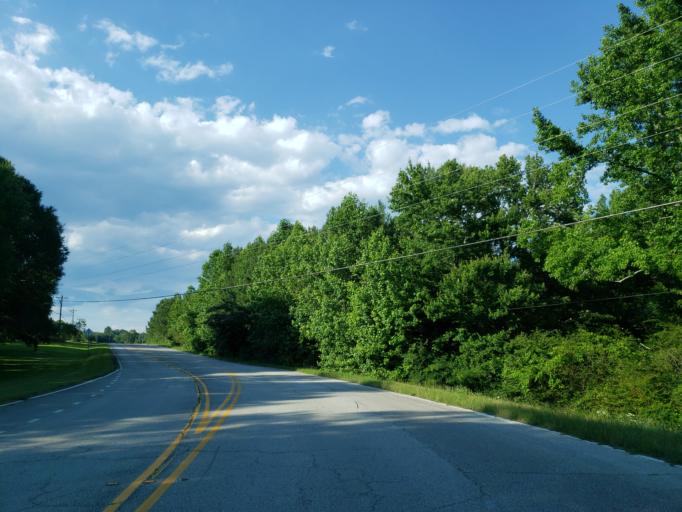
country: US
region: Georgia
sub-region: Haralson County
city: Buchanan
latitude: 33.7725
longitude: -85.1704
